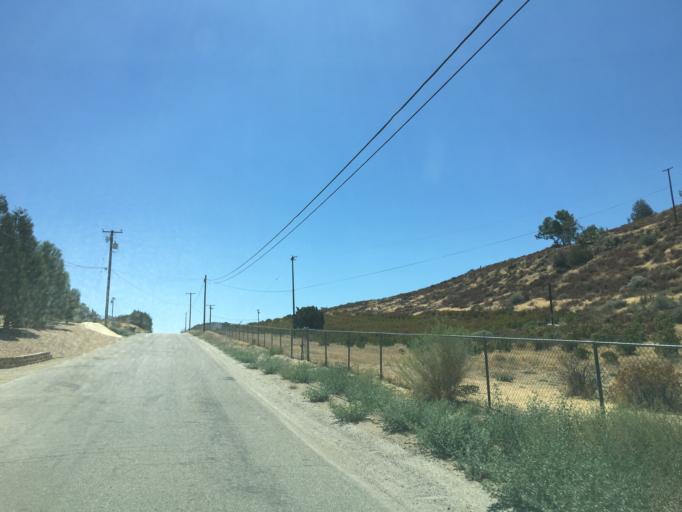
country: US
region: California
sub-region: Los Angeles County
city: Leona Valley
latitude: 34.6250
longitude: -118.2952
